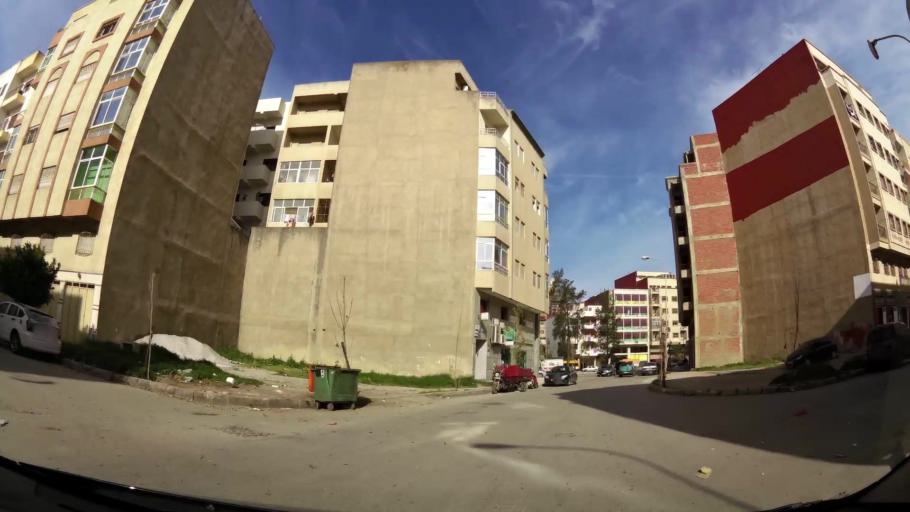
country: MA
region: Tanger-Tetouan
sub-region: Tanger-Assilah
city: Tangier
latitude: 35.7454
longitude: -5.7979
